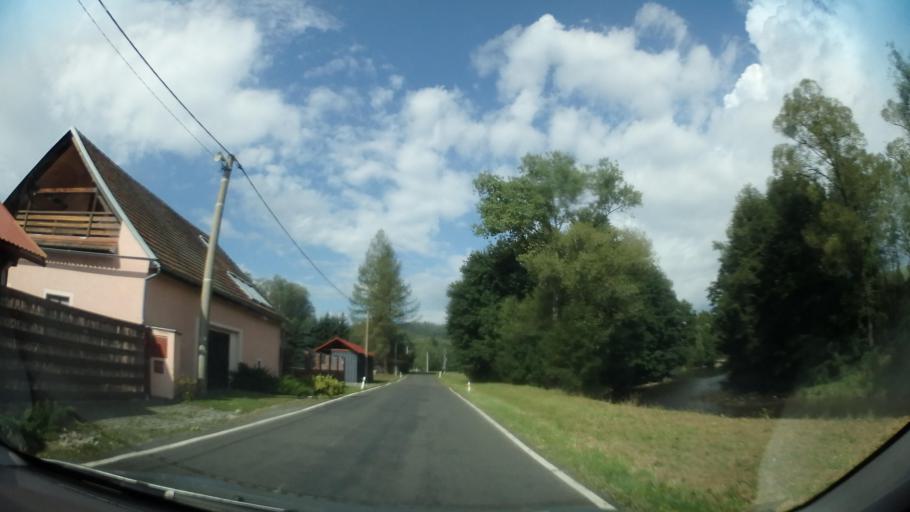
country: CZ
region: Plzensky
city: Horazd'ovice
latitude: 49.2709
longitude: 13.6233
